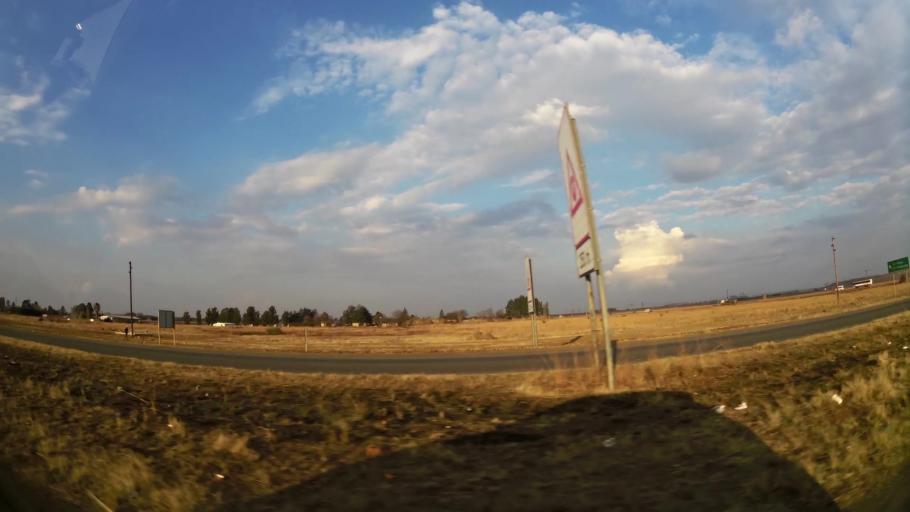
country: ZA
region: Gauteng
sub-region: Sedibeng District Municipality
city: Vanderbijlpark
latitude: -26.6174
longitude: 27.8131
